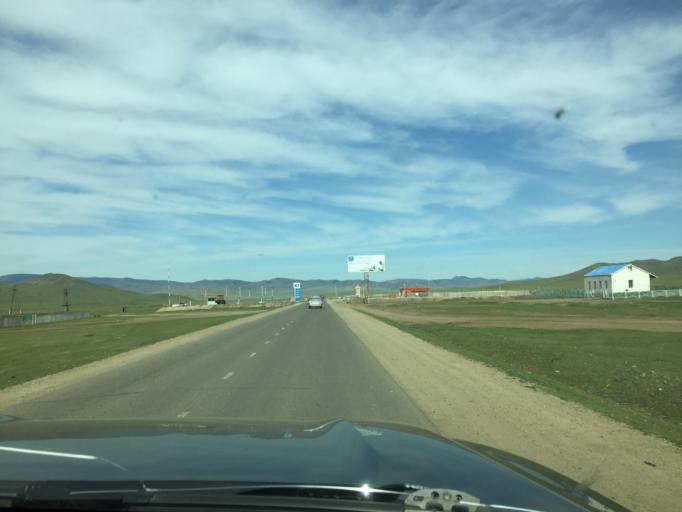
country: MN
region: Central Aimak
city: Ihsueuej
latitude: 48.2278
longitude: 106.2873
